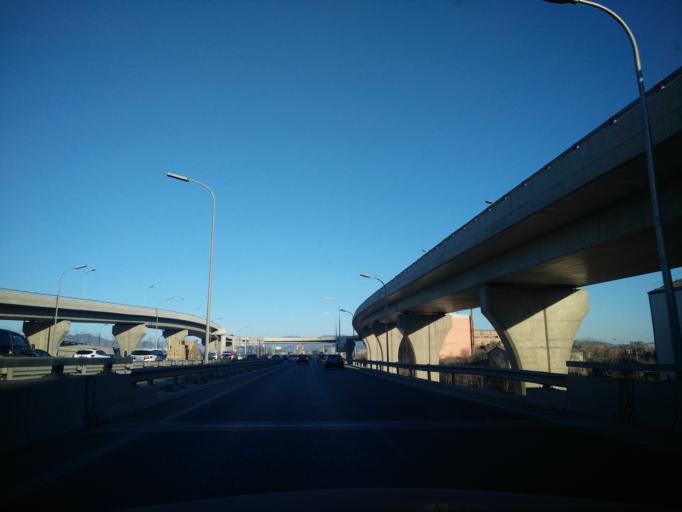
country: CN
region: Beijing
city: Lugu
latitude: 39.8661
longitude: 116.2070
